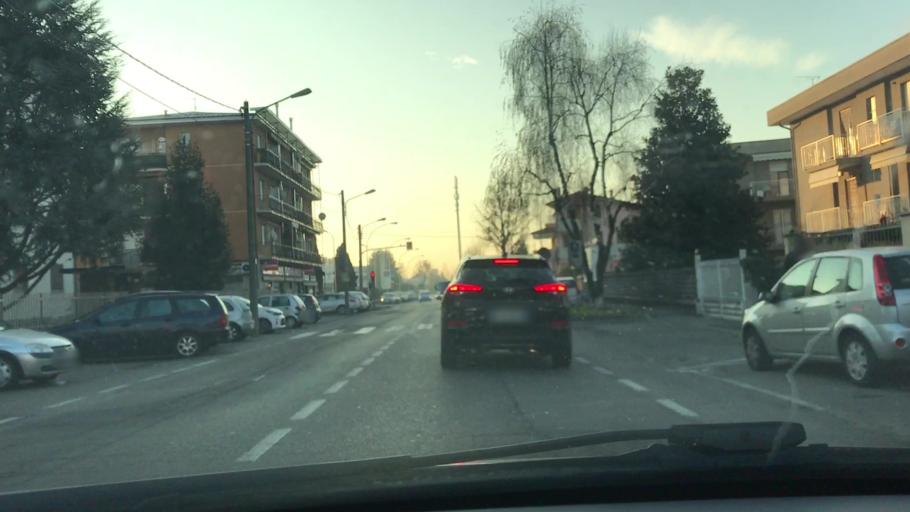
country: IT
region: Lombardy
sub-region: Citta metropolitana di Milano
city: Solaro
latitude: 45.6134
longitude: 9.0916
